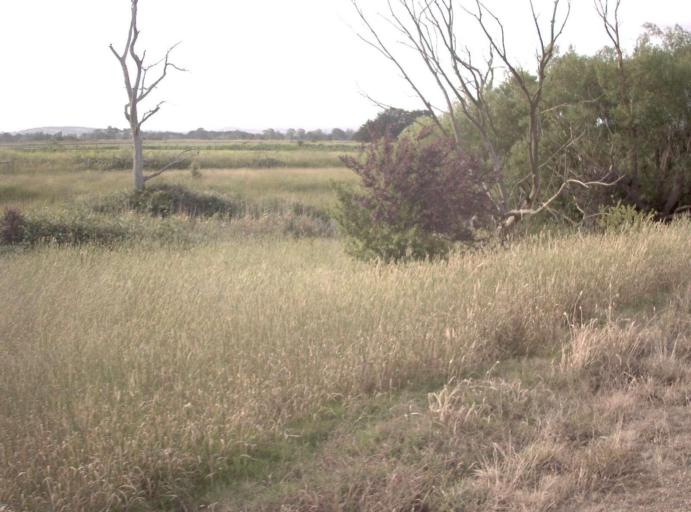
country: AU
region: Victoria
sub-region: Wellington
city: Heyfield
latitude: -37.9750
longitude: 146.8893
